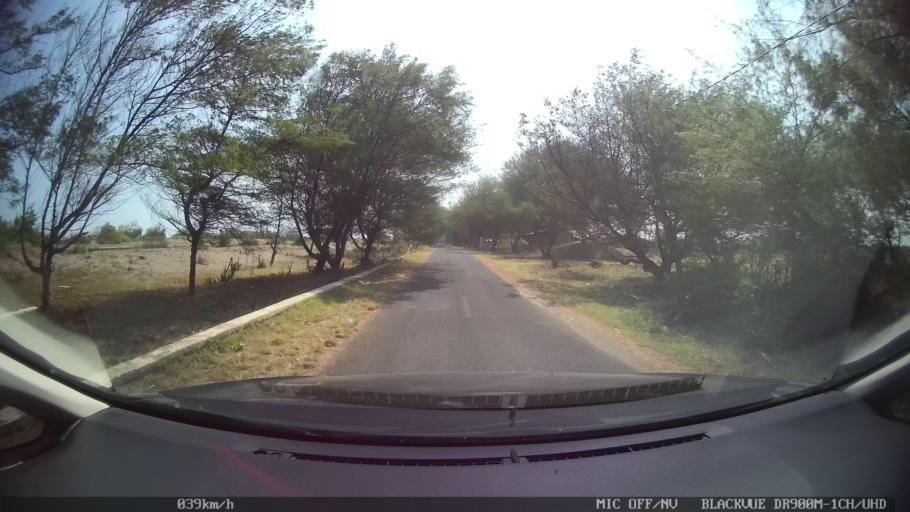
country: ID
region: Daerah Istimewa Yogyakarta
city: Bambanglipuro
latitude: -8.0156
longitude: 110.3021
